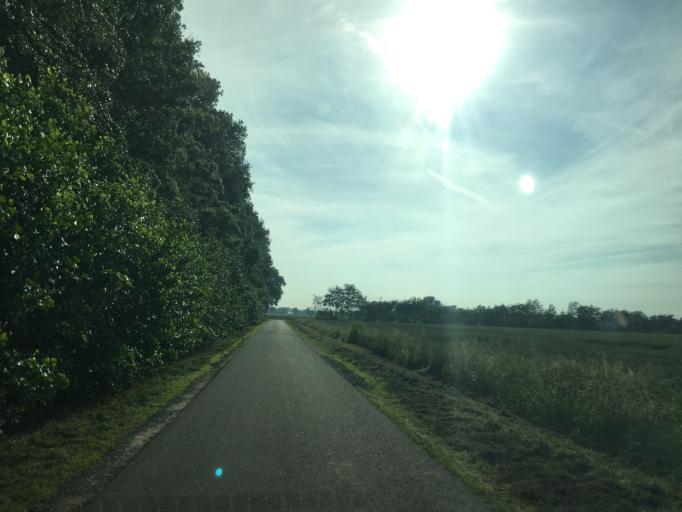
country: DE
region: North Rhine-Westphalia
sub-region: Regierungsbezirk Munster
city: Altenberge
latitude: 52.0006
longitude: 7.5370
